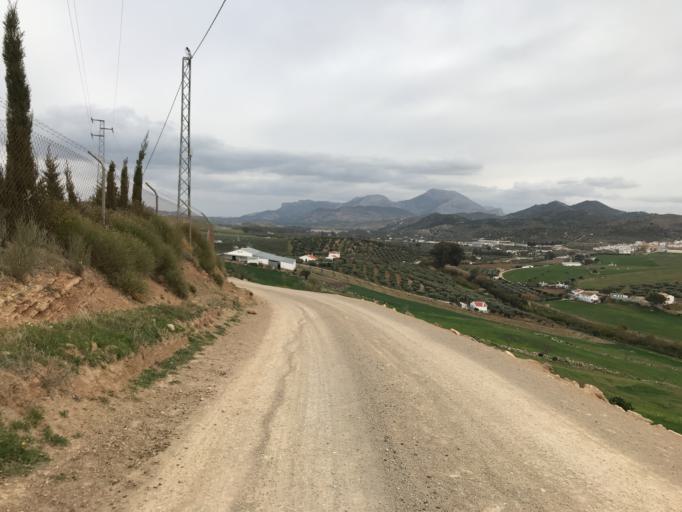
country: ES
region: Andalusia
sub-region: Provincia de Malaga
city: Ardales
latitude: 36.8793
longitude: -4.8639
